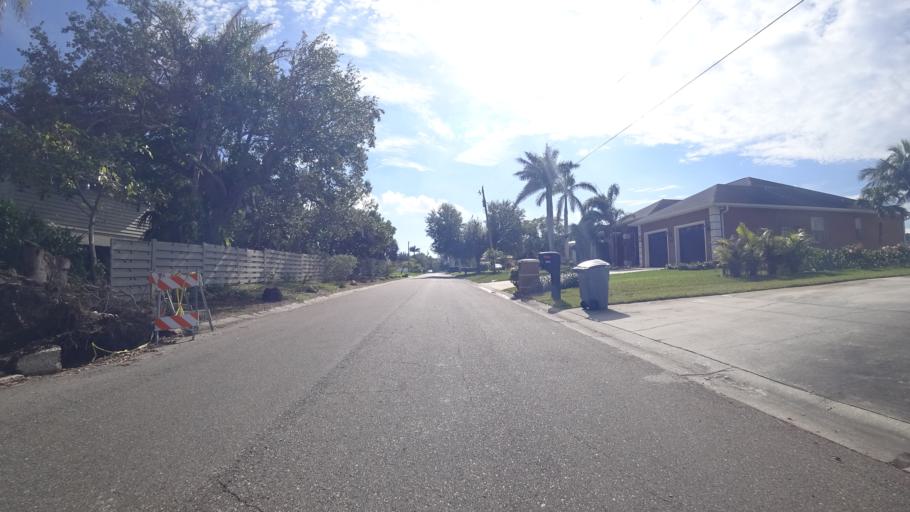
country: US
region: Florida
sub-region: Manatee County
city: West Bradenton
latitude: 27.5185
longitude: -82.6334
